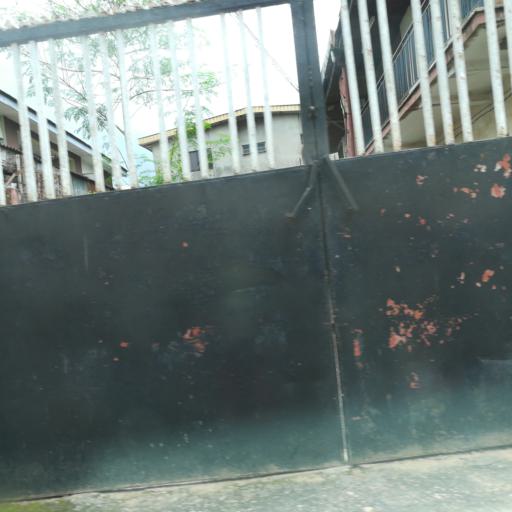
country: NG
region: Lagos
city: Agege
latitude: 6.6028
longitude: 3.2934
